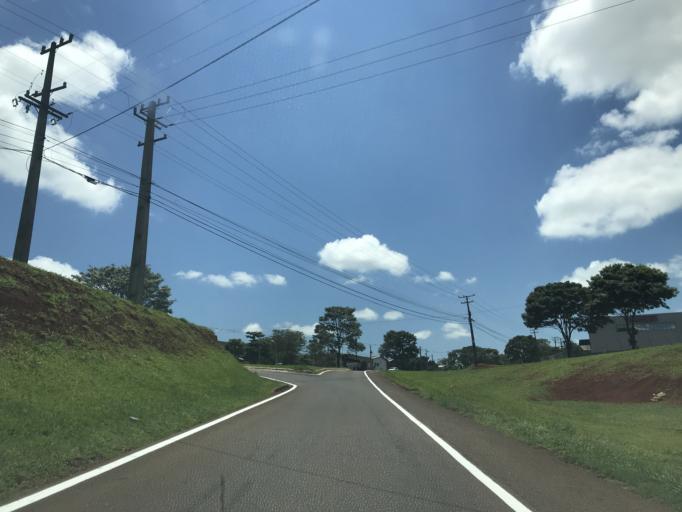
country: BR
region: Parana
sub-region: Marialva
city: Marialva
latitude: -23.4722
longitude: -51.8192
